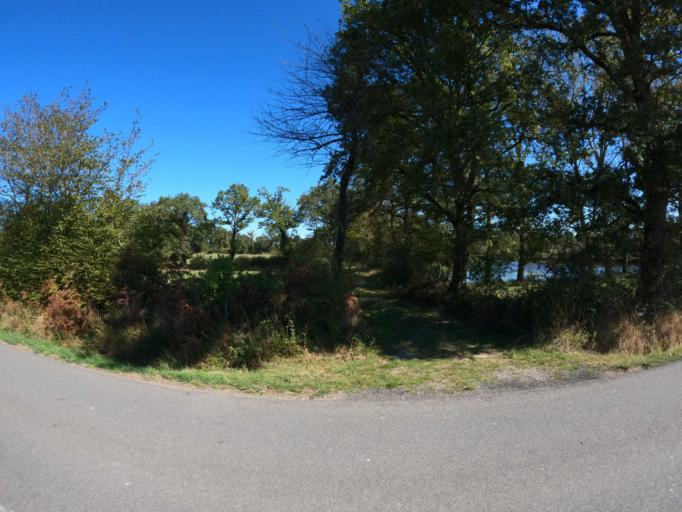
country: FR
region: Poitou-Charentes
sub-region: Departement de la Vienne
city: Lathus-Saint-Remy
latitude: 46.2748
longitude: 1.0196
